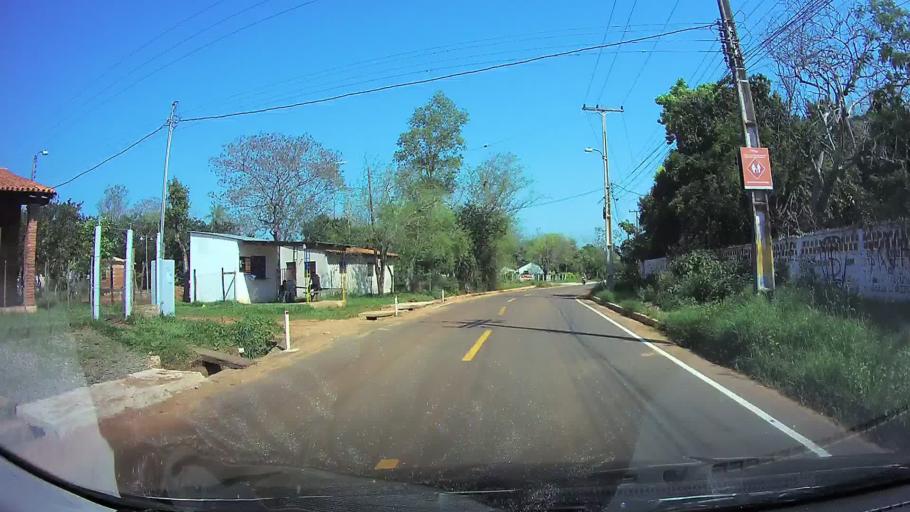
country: PY
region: Central
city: Limpio
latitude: -25.2337
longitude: -57.4905
